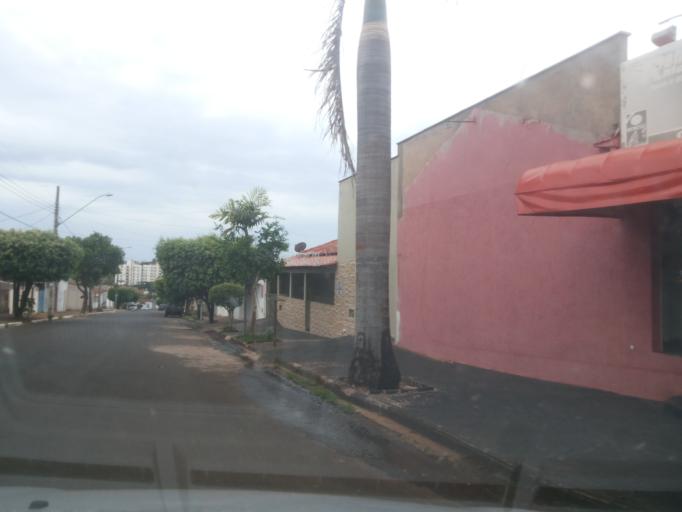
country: BR
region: Minas Gerais
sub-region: Ituiutaba
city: Ituiutaba
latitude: -18.9703
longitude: -49.4731
